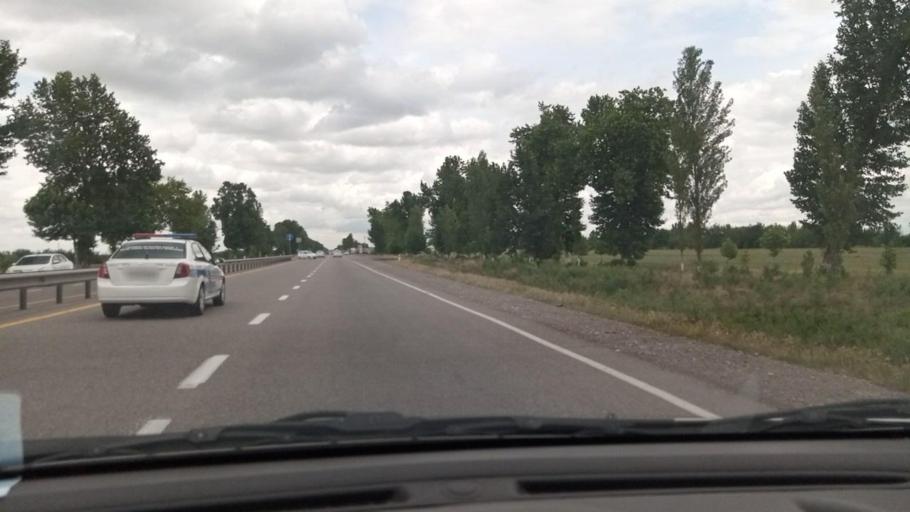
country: UZ
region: Toshkent Shahri
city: Bektemir
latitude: 41.2035
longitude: 69.4030
